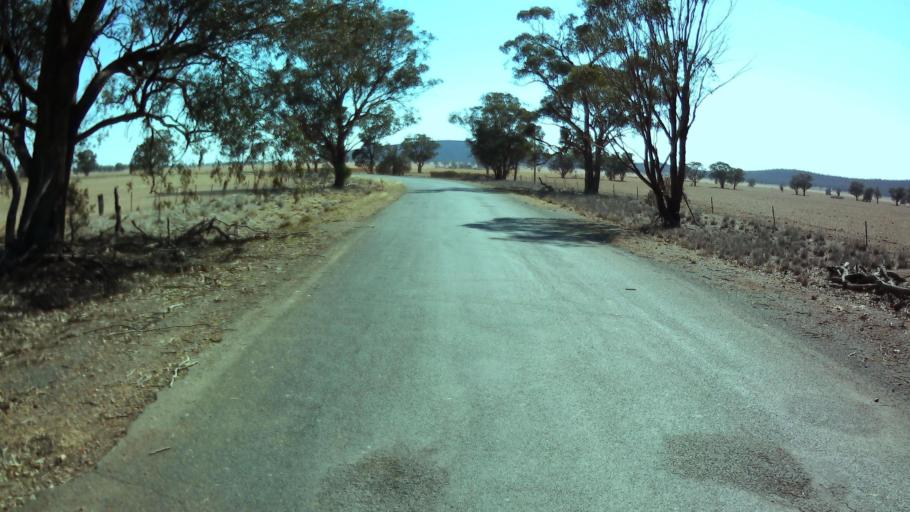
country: AU
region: New South Wales
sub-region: Weddin
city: Grenfell
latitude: -33.7061
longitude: 147.9170
